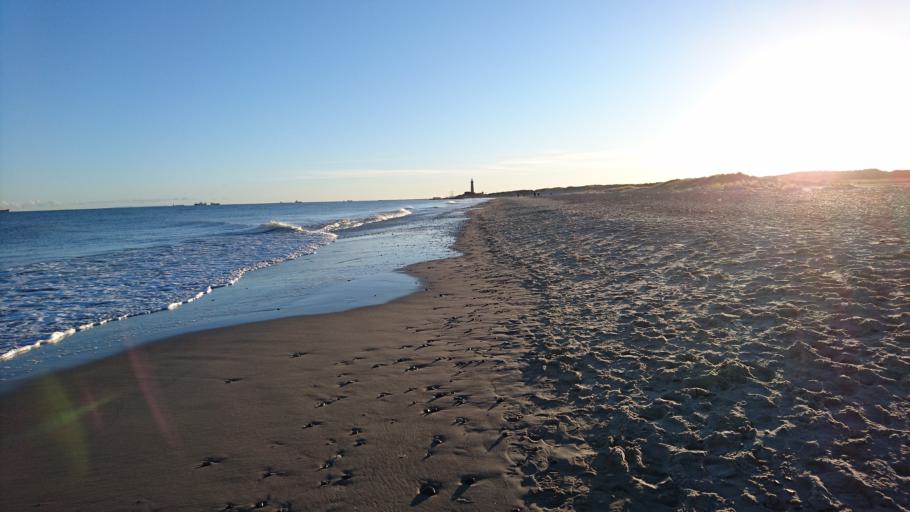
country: DK
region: North Denmark
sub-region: Frederikshavn Kommune
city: Skagen
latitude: 57.7439
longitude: 10.6477
